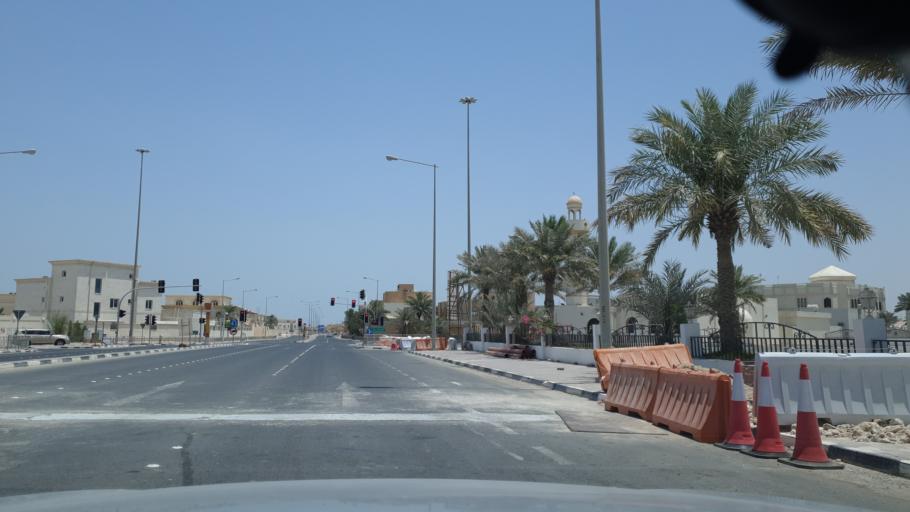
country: QA
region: Baladiyat Umm Salal
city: Umm Salal Muhammad
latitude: 25.3645
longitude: 51.4349
